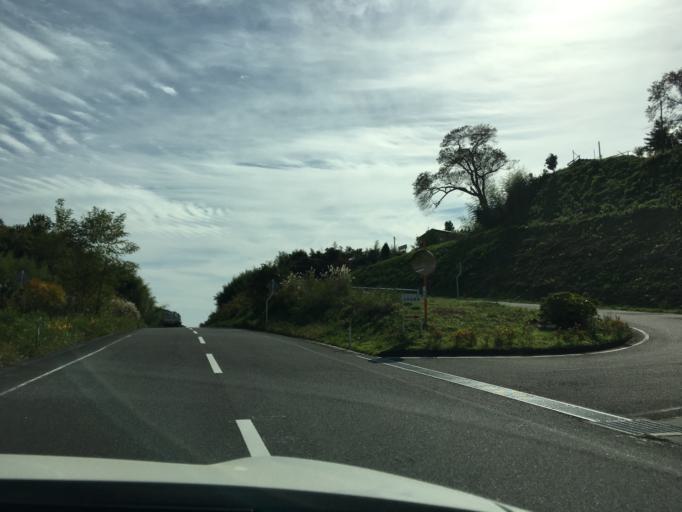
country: JP
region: Fukushima
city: Nihommatsu
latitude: 37.5548
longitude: 140.4994
